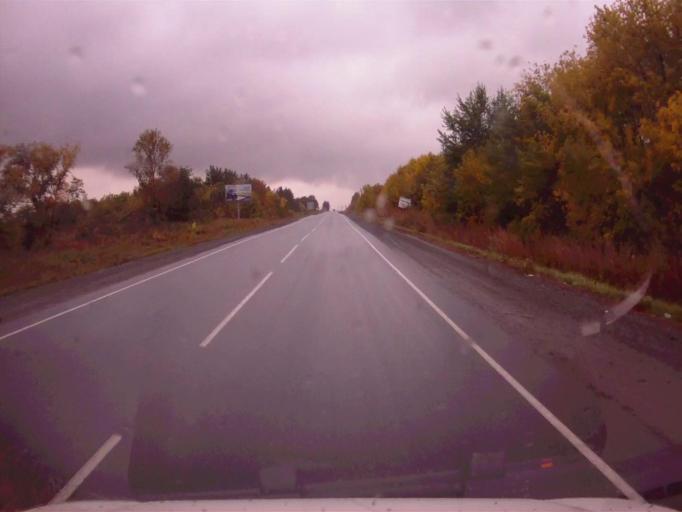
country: RU
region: Chelyabinsk
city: Roshchino
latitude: 55.3700
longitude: 61.1757
